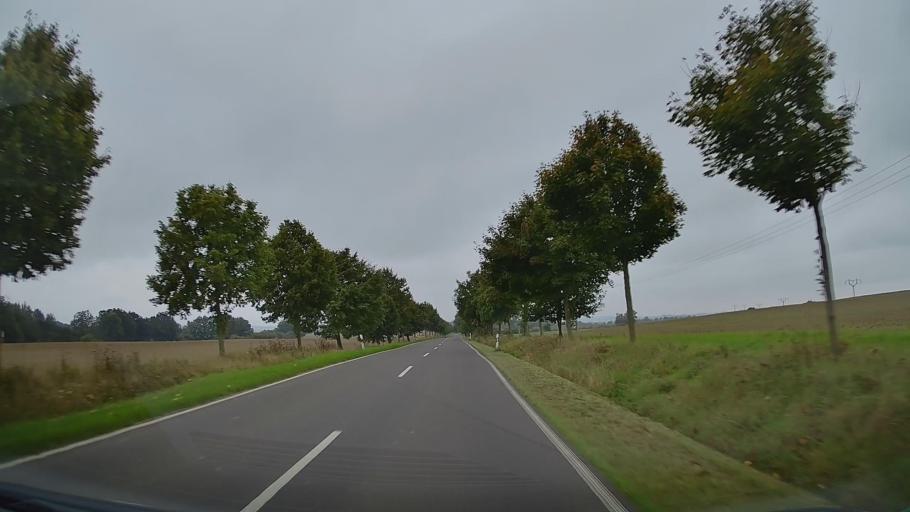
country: DE
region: Mecklenburg-Vorpommern
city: Guestrow
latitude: 53.8002
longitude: 12.1020
